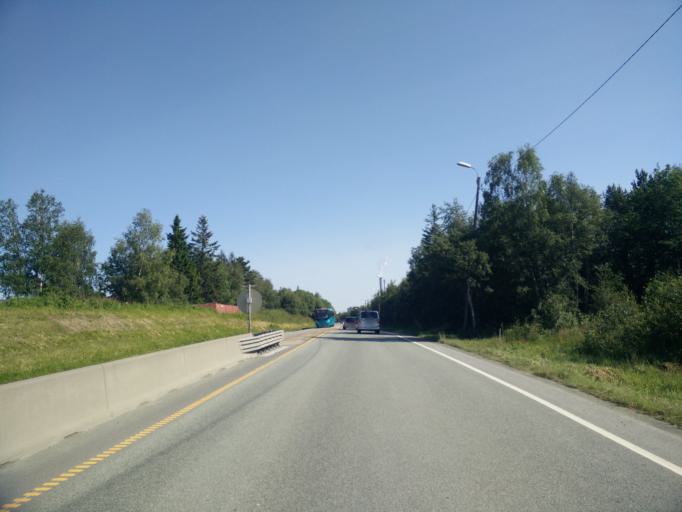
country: NO
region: Sor-Trondelag
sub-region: Trondheim
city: Trondheim
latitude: 63.3402
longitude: 10.3637
